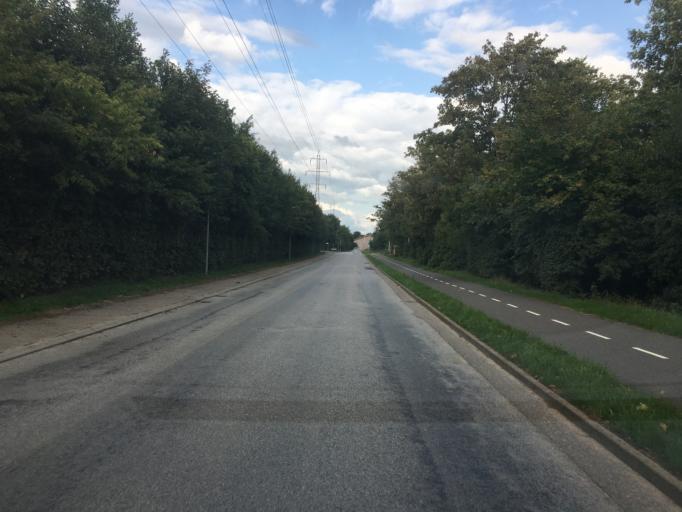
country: DK
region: South Denmark
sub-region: Tonder Kommune
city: Tonder
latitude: 54.9348
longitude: 8.8804
